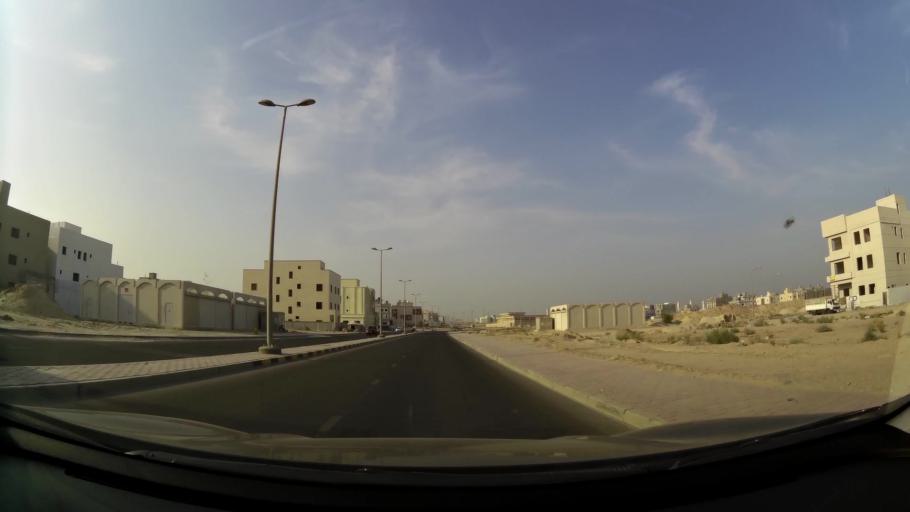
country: KW
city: Al Funaytis
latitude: 29.2236
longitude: 48.0918
